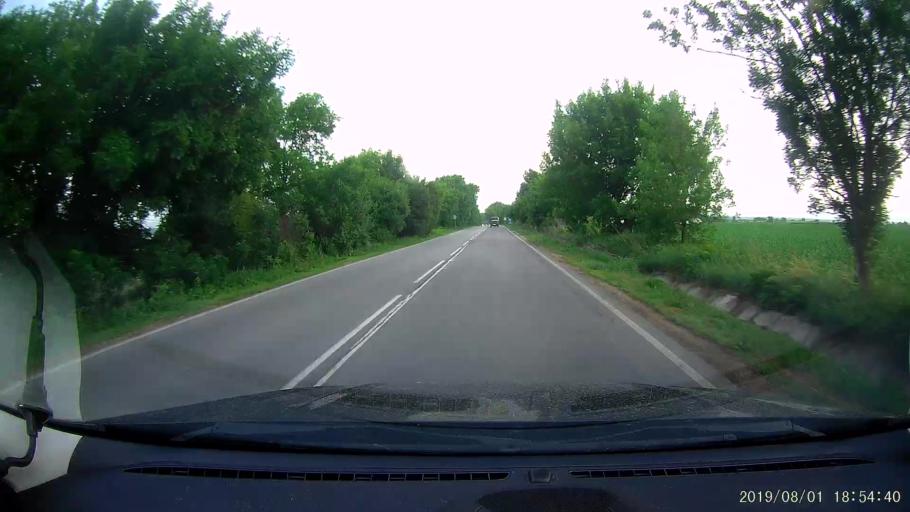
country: BG
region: Shumen
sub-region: Obshtina Shumen
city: Shumen
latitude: 43.1931
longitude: 27.0029
